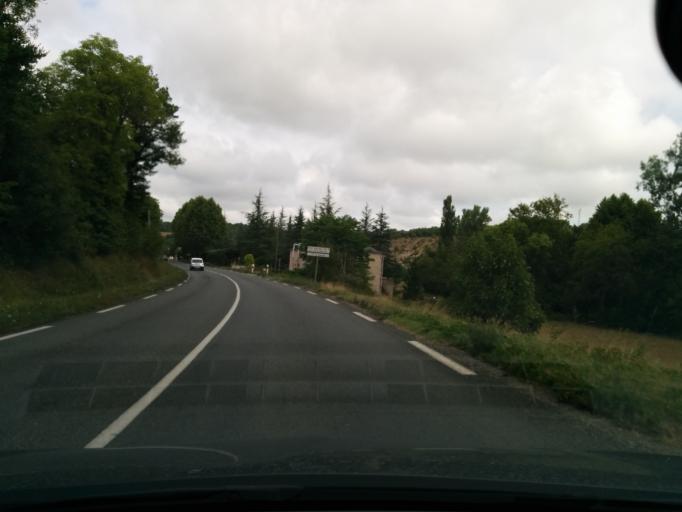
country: FR
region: Midi-Pyrenees
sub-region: Departement du Lot
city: Le Vigan
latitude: 44.6685
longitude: 1.4810
